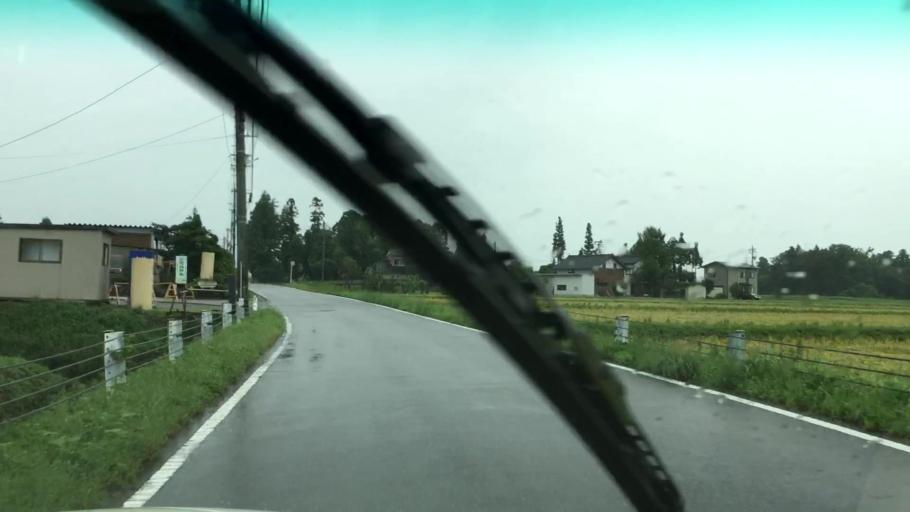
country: JP
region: Toyama
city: Kamiichi
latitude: 36.6750
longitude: 137.3210
